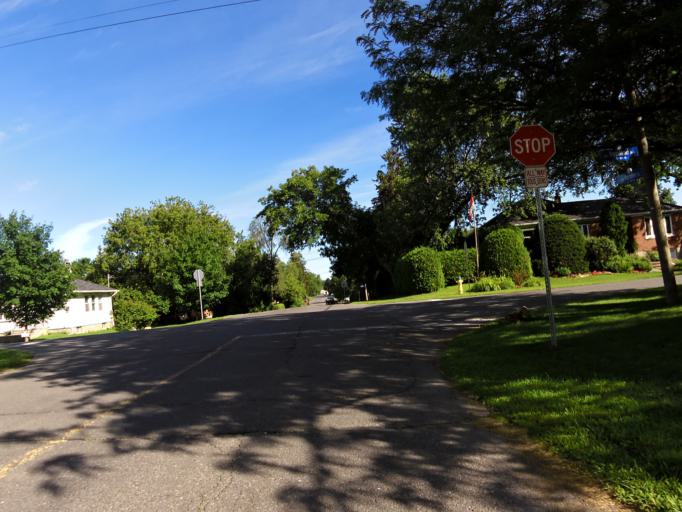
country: CA
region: Ontario
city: Ottawa
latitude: 45.3528
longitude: -75.7399
